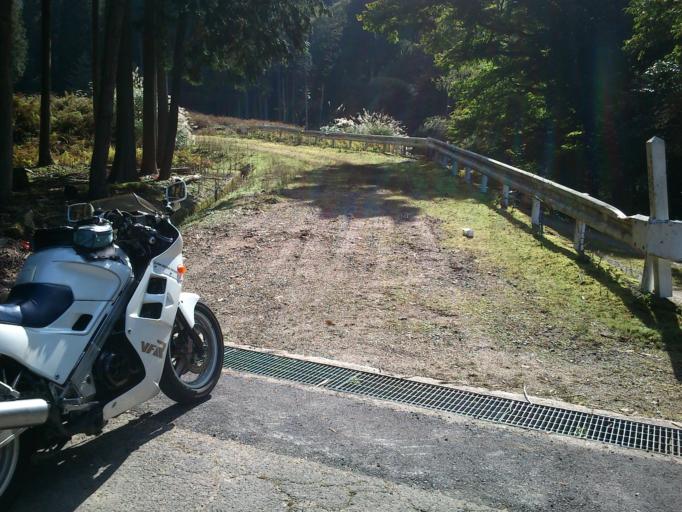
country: JP
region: Kyoto
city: Miyazu
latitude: 35.5446
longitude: 135.0189
